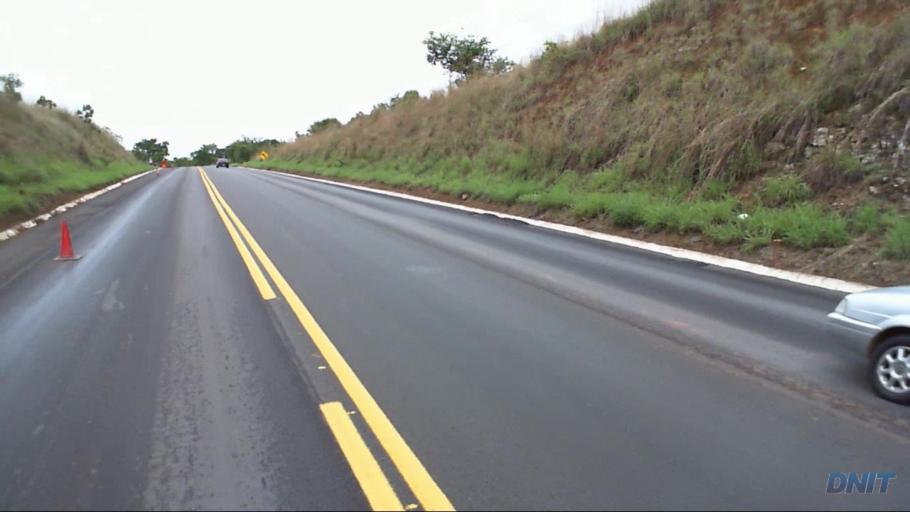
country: BR
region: Goias
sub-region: Padre Bernardo
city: Padre Bernardo
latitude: -15.1793
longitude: -48.4228
